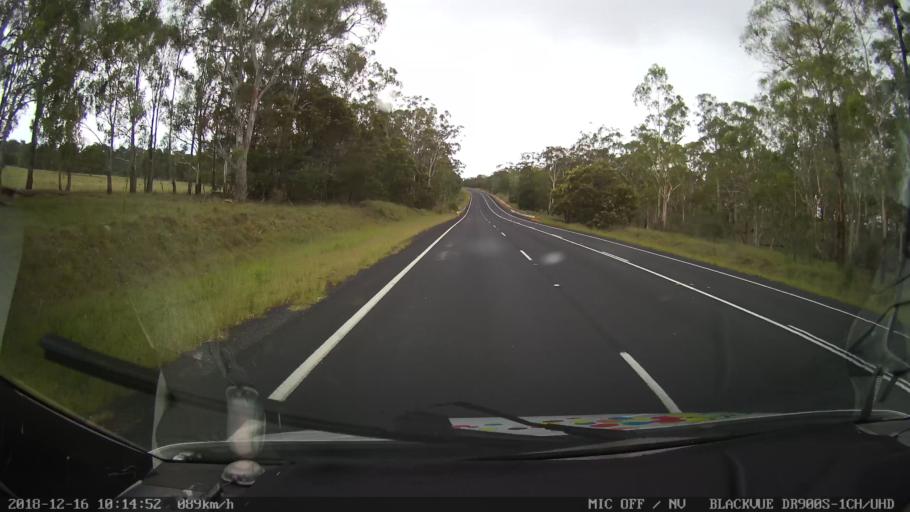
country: AU
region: New South Wales
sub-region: Tenterfield Municipality
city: Carrolls Creek
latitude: -29.2826
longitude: 151.9668
